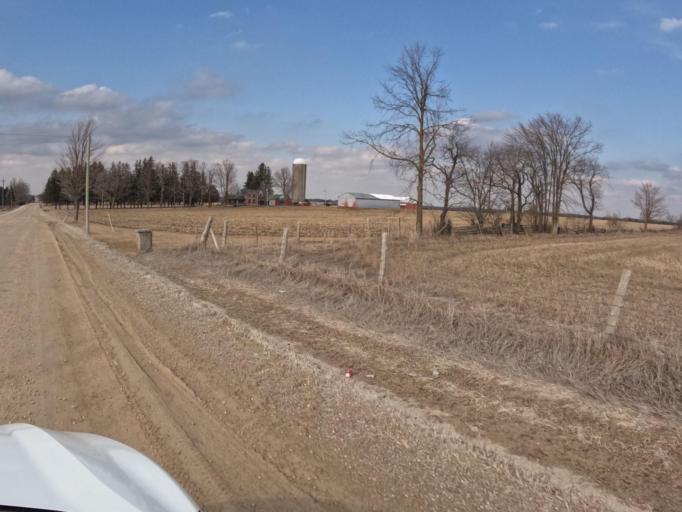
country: CA
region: Ontario
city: Orangeville
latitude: 43.8828
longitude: -80.2973
